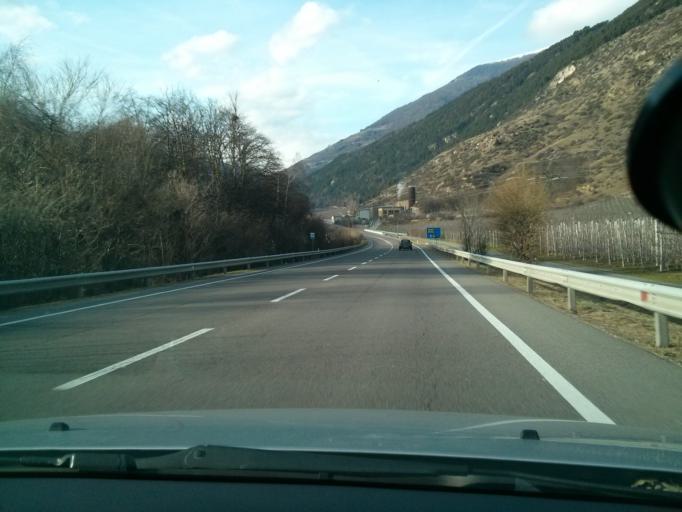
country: IT
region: Trentino-Alto Adige
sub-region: Bolzano
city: Lasa
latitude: 46.6239
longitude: 10.6950
